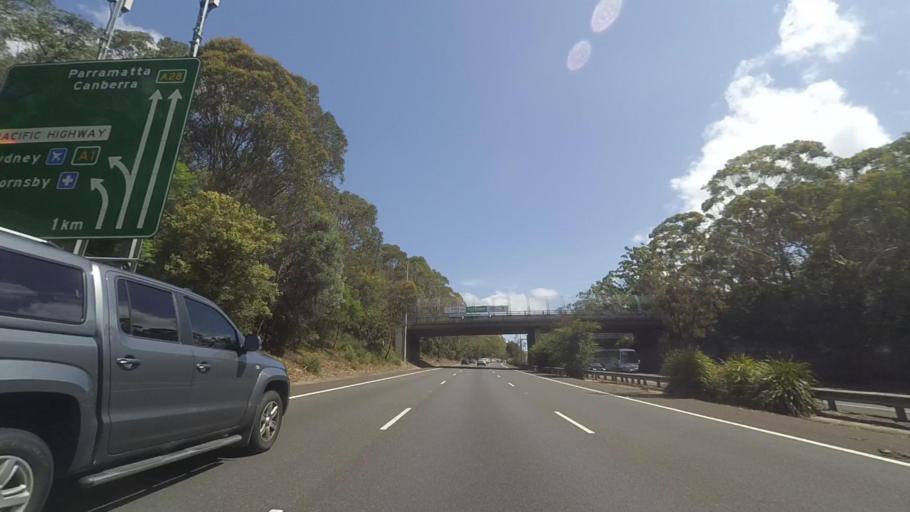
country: AU
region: New South Wales
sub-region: Ku-ring-gai
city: North Wahroonga
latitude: -33.7078
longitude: 151.1175
